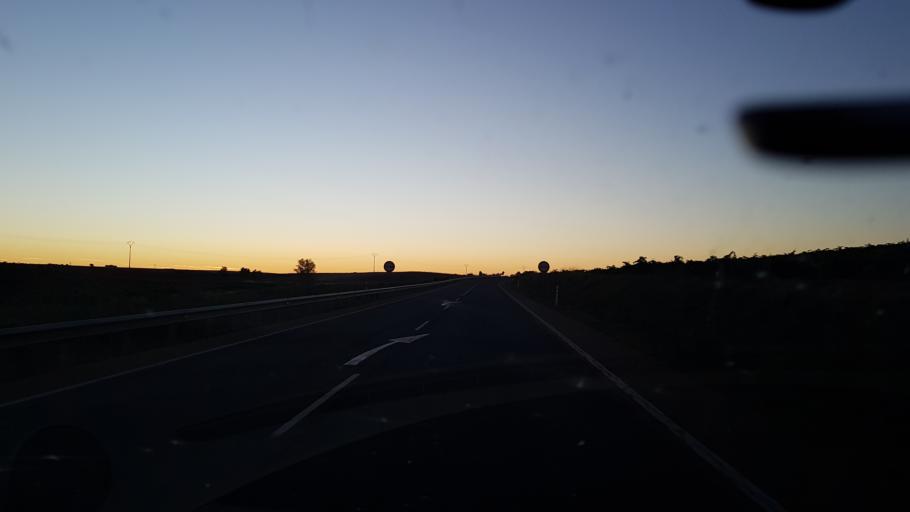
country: ES
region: Castille and Leon
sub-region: Provincia de Valladolid
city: San Roman de Hornija
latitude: 41.5212
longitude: -5.2617
